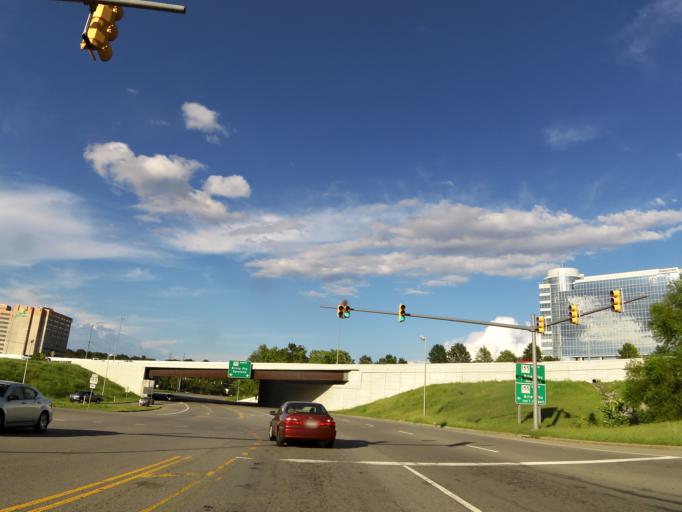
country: US
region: Tennessee
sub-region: Davidson County
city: Nashville
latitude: 36.1511
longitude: -86.6921
